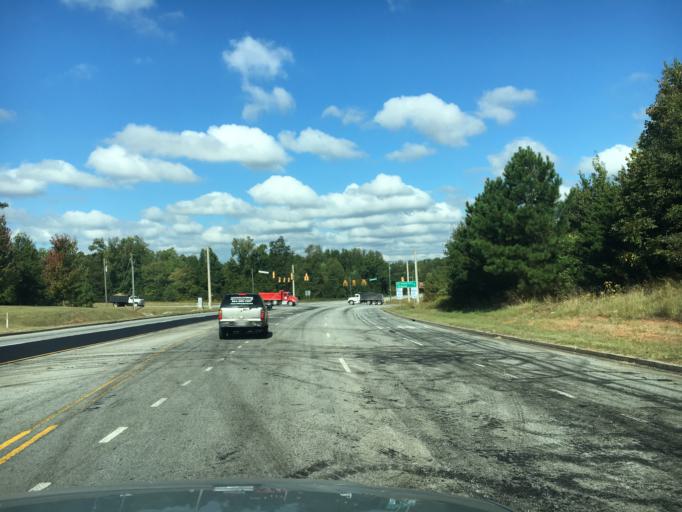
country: US
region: South Carolina
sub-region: Greenville County
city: Greer
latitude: 34.9120
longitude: -82.2086
